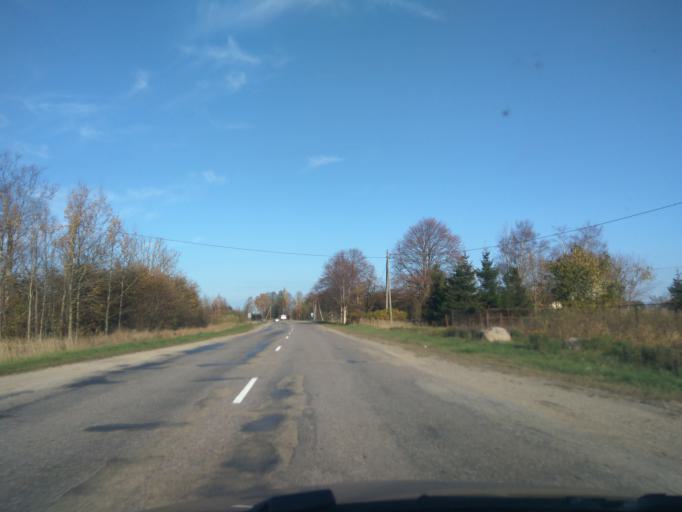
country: LV
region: Ventspils
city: Ventspils
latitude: 57.3403
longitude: 21.5677
